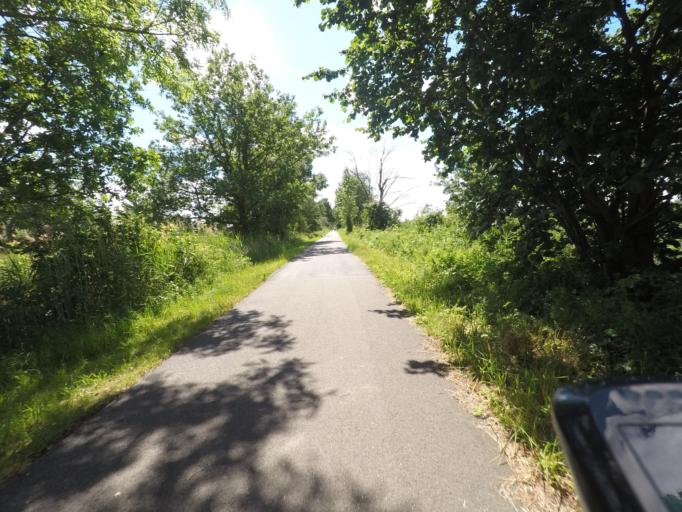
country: DE
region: Hamburg
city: Bergedorf
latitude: 53.4396
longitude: 10.2145
